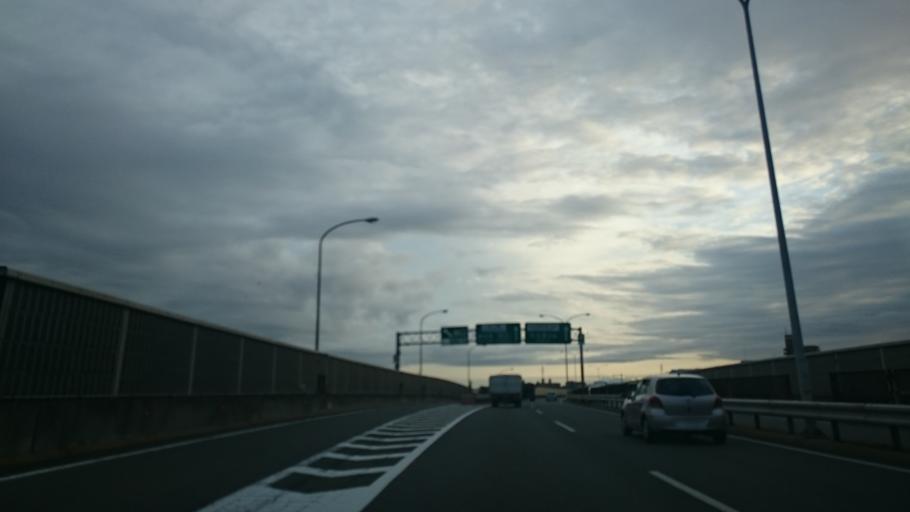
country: JP
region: Aichi
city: Kanie
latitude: 35.1567
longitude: 136.8094
